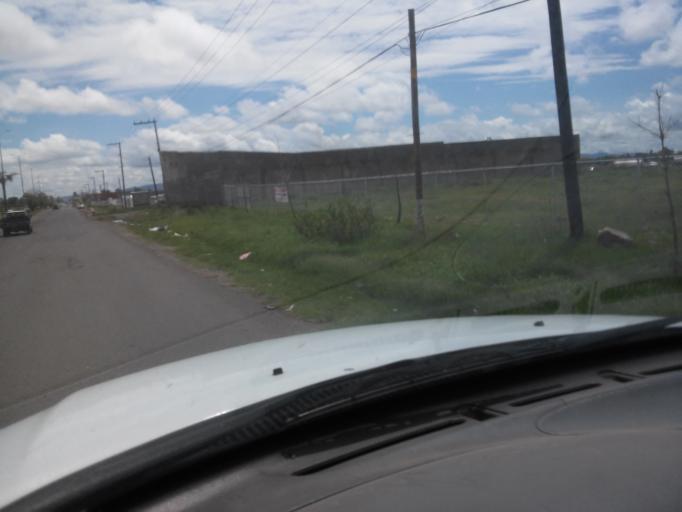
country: MX
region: Durango
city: Victoria de Durango
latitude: 24.0290
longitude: -104.6001
